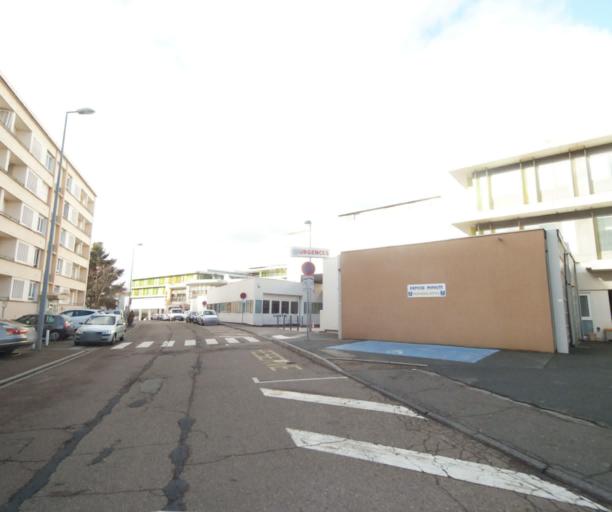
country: FR
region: Rhone-Alpes
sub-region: Departement de la Loire
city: Roanne
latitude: 46.0423
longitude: 4.0797
